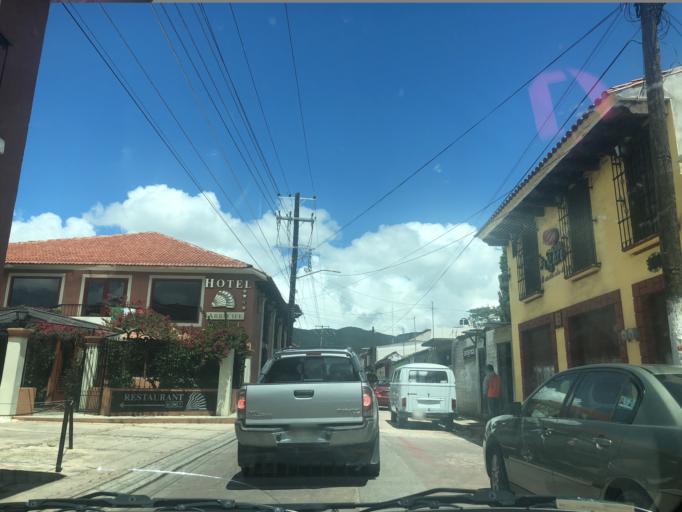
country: MX
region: Chiapas
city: San Cristobal de las Casas
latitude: 16.7325
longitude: -92.6391
